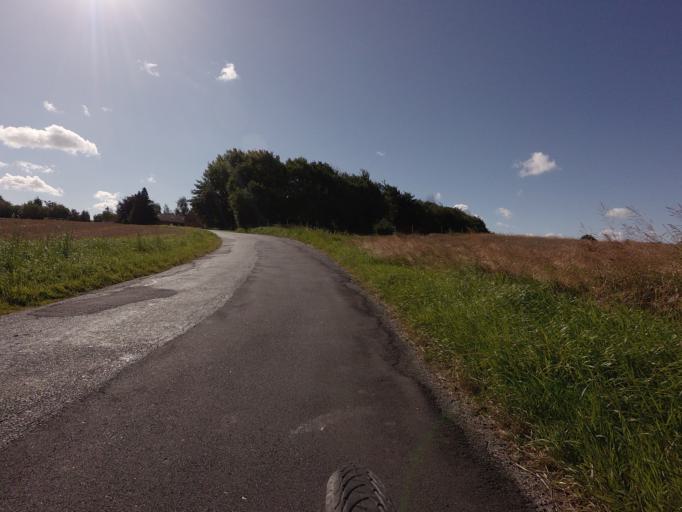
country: DK
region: Central Jutland
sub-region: Horsens Kommune
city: Braedstrup
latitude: 55.9714
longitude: 9.7133
